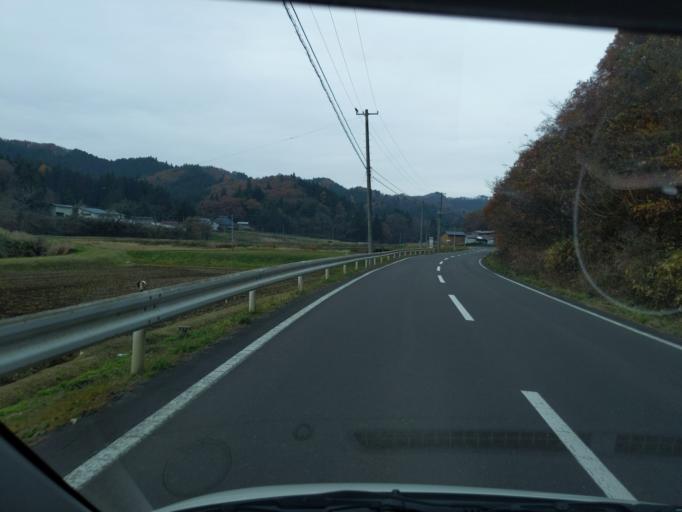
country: JP
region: Iwate
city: Kitakami
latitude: 39.2611
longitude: 141.1871
